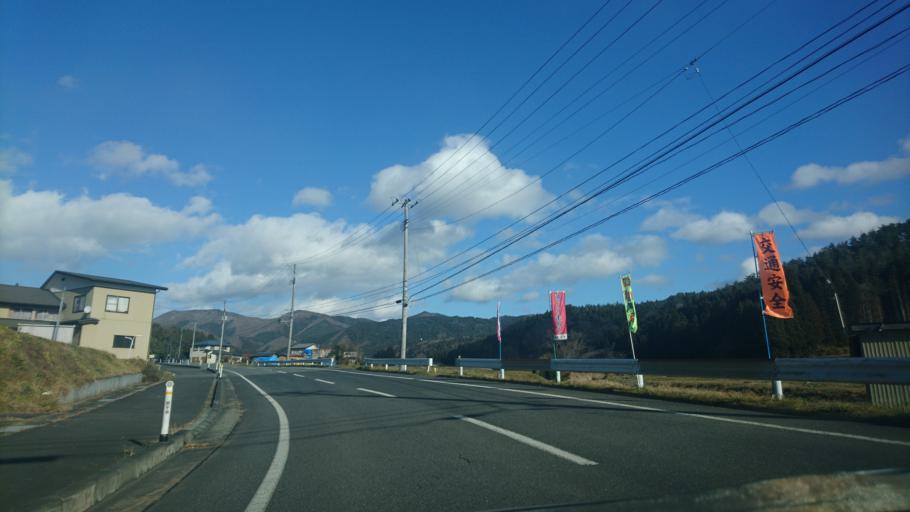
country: JP
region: Iwate
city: Mizusawa
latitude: 39.0596
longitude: 141.3717
